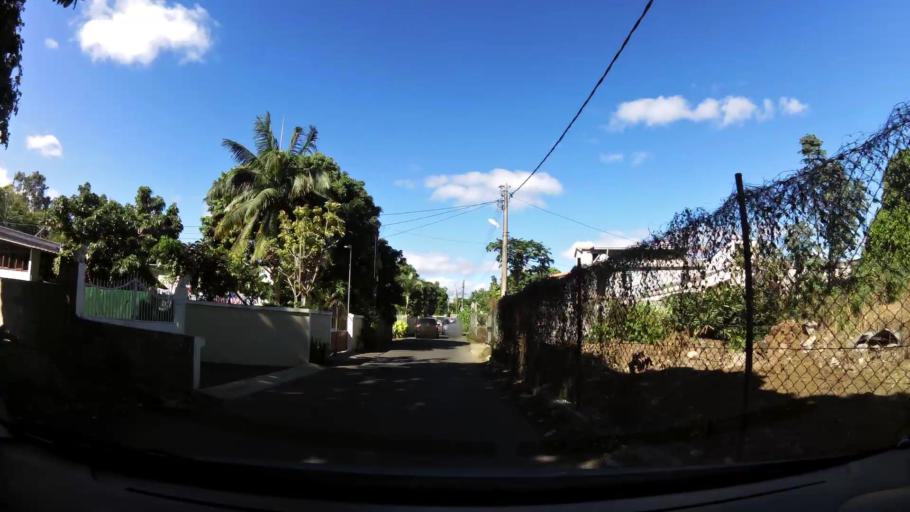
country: MU
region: Plaines Wilhems
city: Vacoas
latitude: -20.2829
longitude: 57.4639
